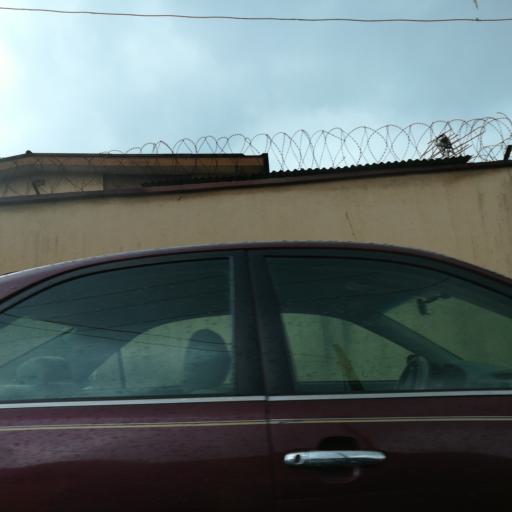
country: NG
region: Lagos
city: Agege
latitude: 6.5894
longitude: 3.2954
